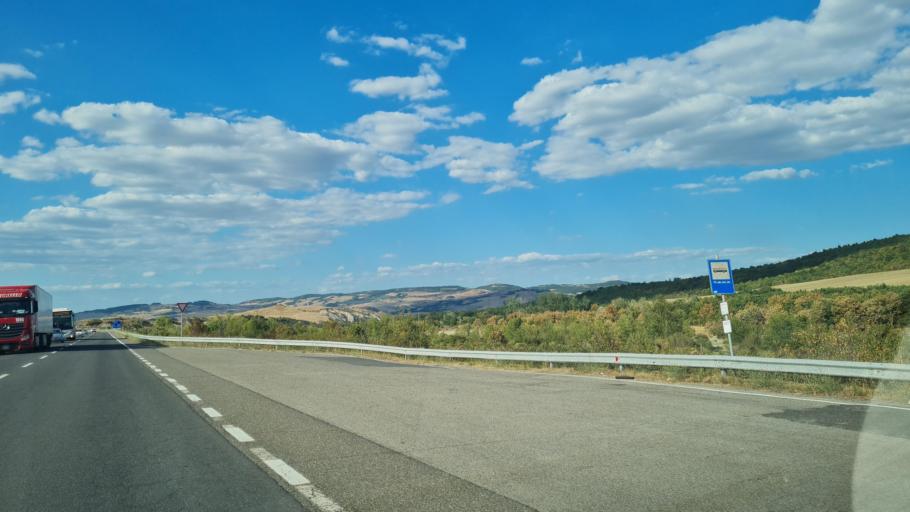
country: IT
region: Tuscany
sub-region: Provincia di Siena
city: Castiglione d'Orcia
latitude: 42.9747
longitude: 11.7062
